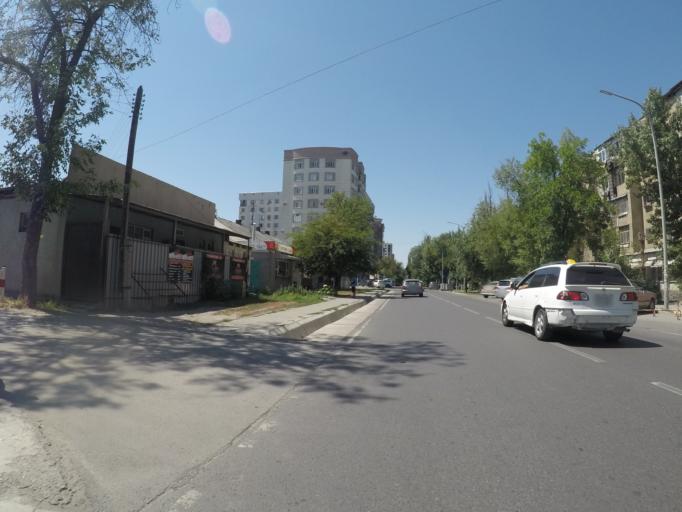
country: KG
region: Chuy
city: Bishkek
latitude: 42.8679
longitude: 74.5832
